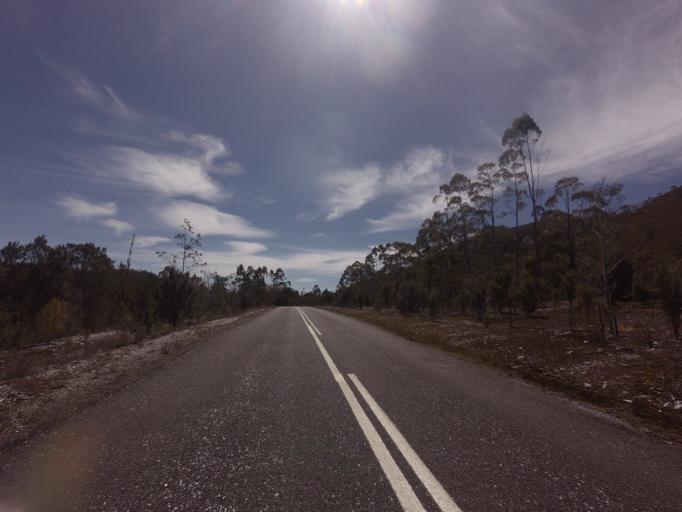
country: AU
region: Tasmania
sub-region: West Coast
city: Queenstown
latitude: -42.7684
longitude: 146.0563
